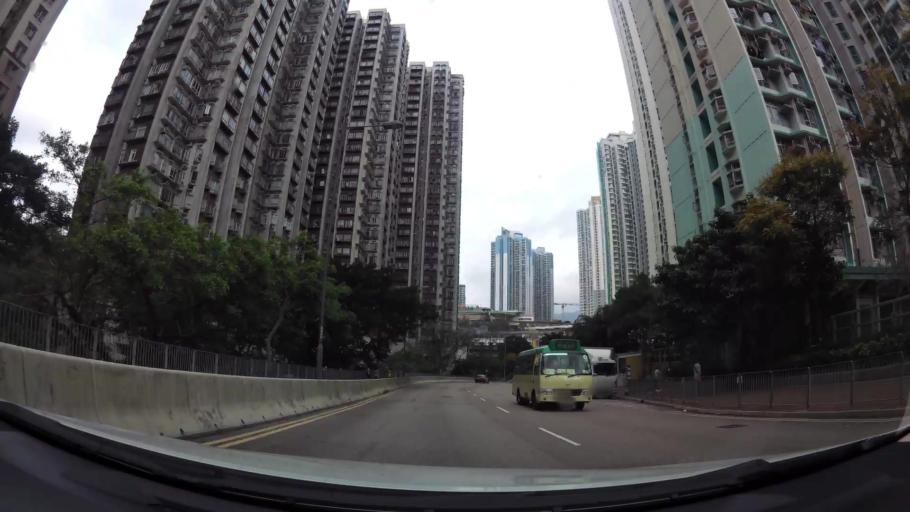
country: HK
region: Kowloon City
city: Kowloon
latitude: 22.3266
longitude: 114.2154
